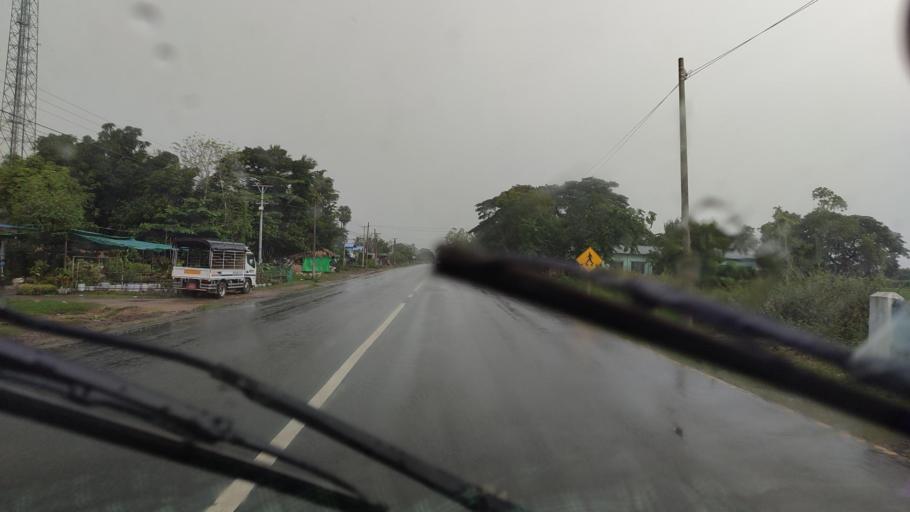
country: MM
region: Bago
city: Bago
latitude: 17.5751
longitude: 96.5534
